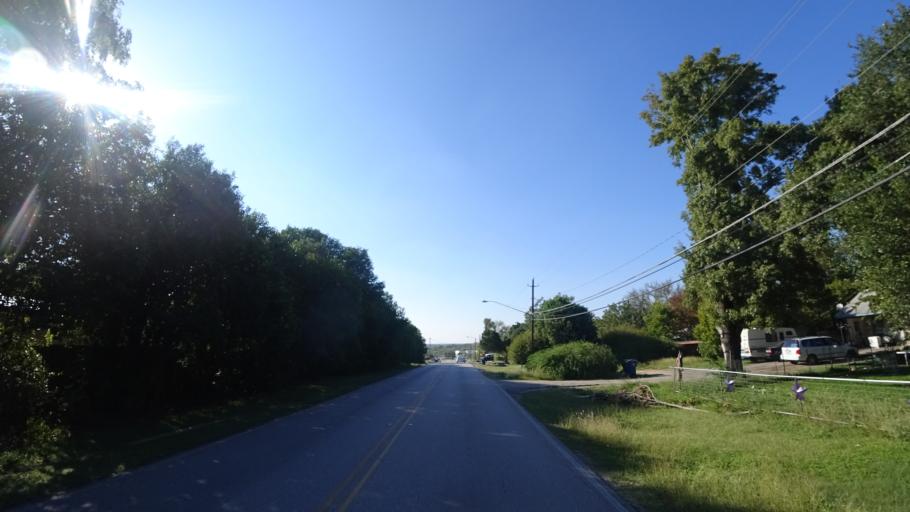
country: US
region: Texas
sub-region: Travis County
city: Wells Branch
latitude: 30.3444
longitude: -97.6732
